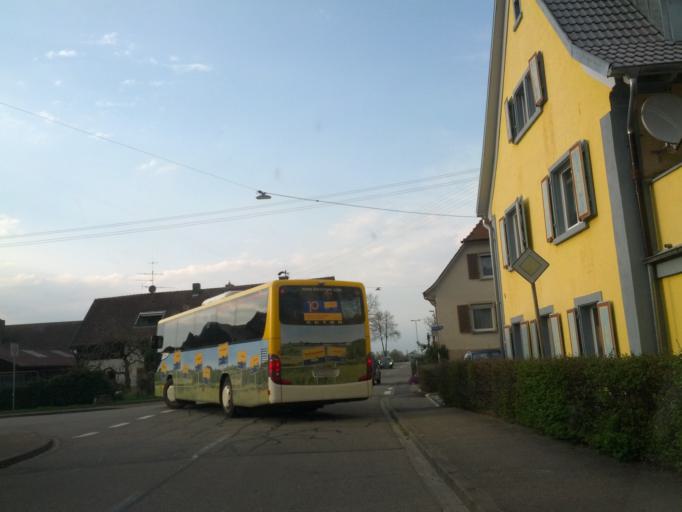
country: DE
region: Baden-Wuerttemberg
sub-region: Freiburg Region
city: Eichstetten
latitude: 48.1064
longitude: 7.7780
